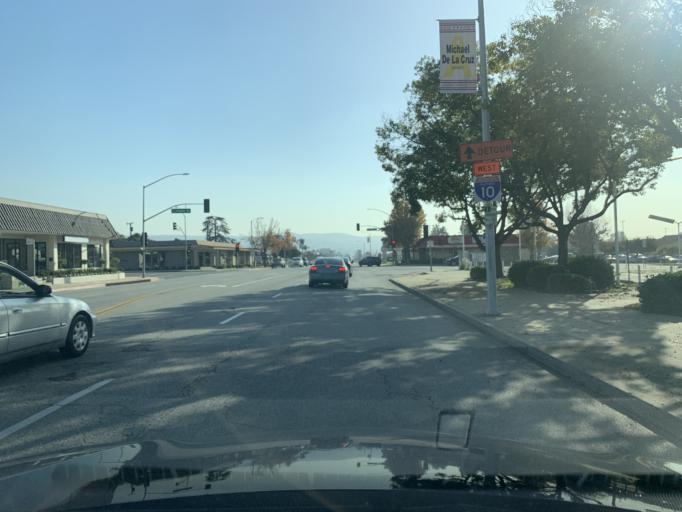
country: US
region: California
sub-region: Los Angeles County
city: Covina
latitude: 34.0833
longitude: -117.8902
